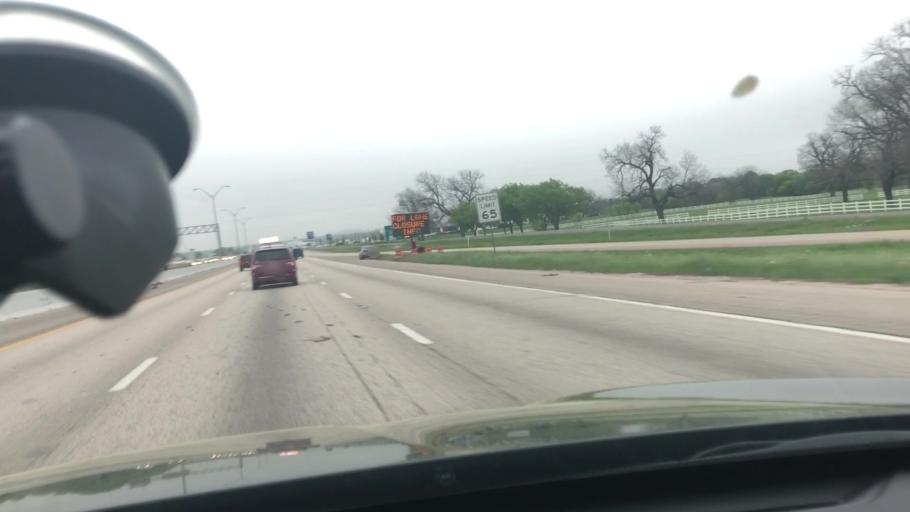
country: US
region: Texas
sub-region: Bell County
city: Belton
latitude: 31.0579
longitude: -97.4429
